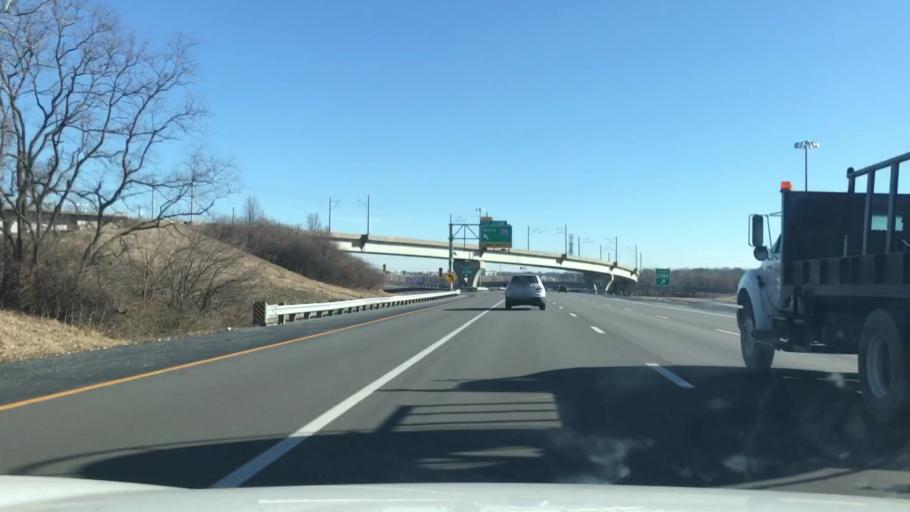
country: US
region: Missouri
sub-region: Saint Louis County
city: Saint Johns
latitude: 38.7305
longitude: -90.3358
